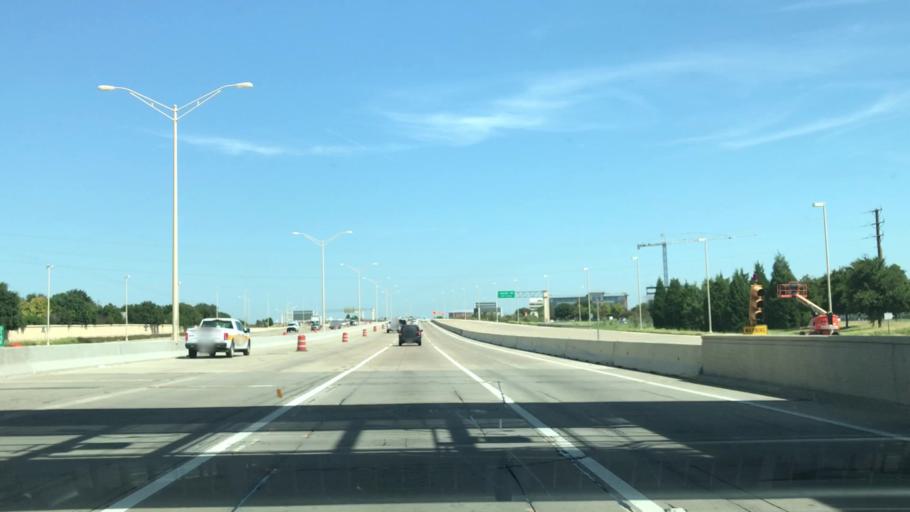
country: US
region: Texas
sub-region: Collin County
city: Plano
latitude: 32.9894
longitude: -96.6672
